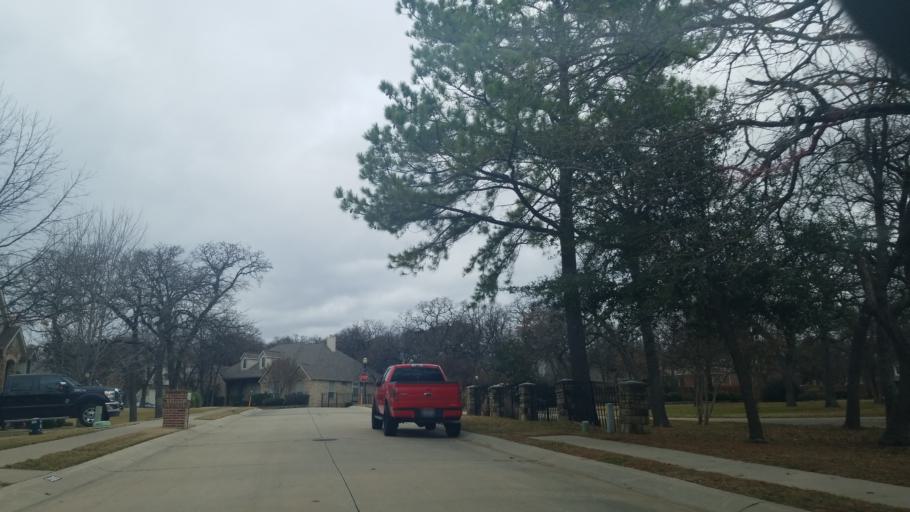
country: US
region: Texas
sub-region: Denton County
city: Corinth
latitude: 33.1330
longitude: -97.0810
